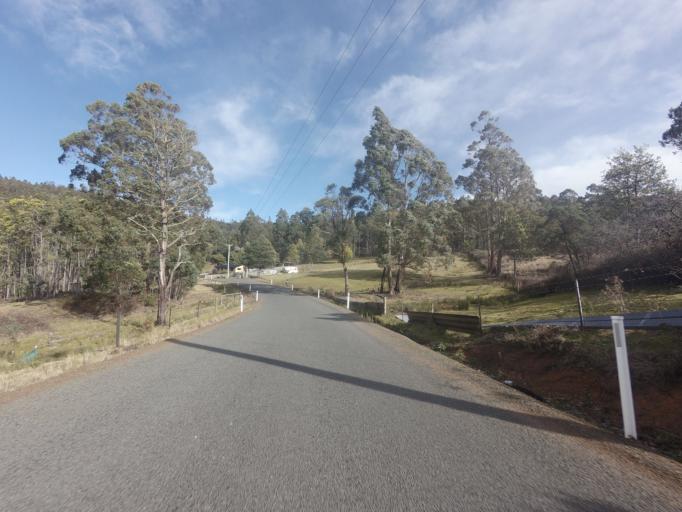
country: AU
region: Tasmania
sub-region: Kingborough
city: Margate
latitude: -43.0123
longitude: 147.1611
